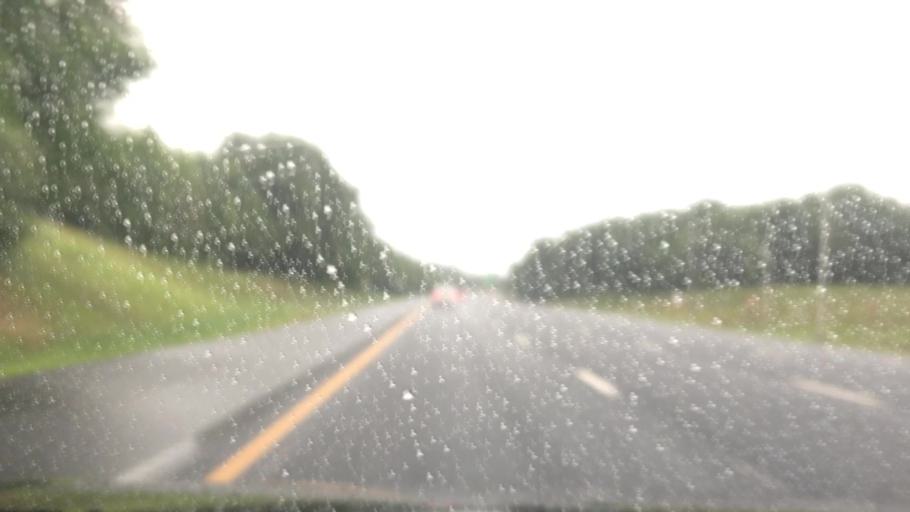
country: US
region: New Jersey
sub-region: Monmouth County
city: Shark River Hills
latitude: 40.2137
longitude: -74.0976
